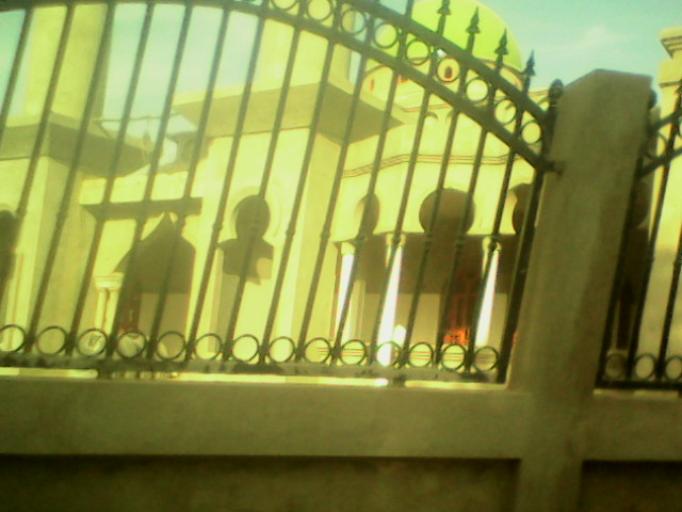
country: SN
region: Diourbel
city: Touba
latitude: 14.8499
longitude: -15.8809
